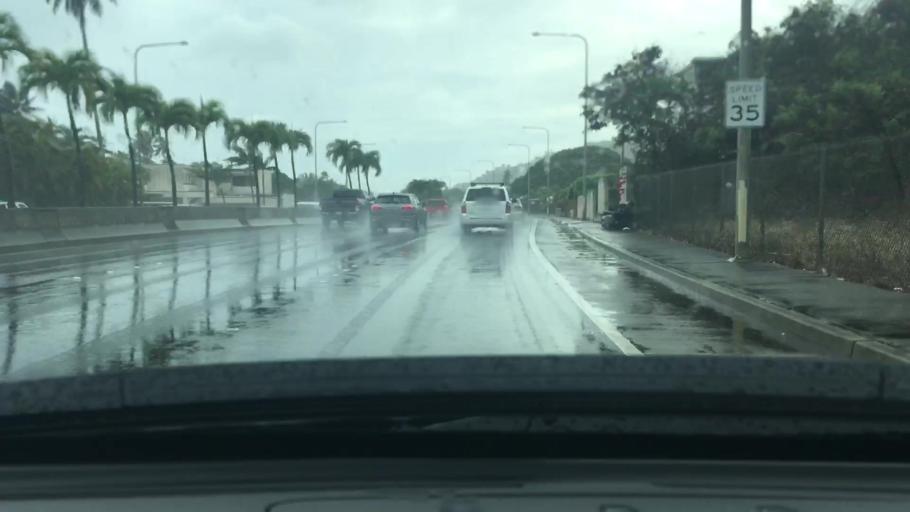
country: US
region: Hawaii
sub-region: Honolulu County
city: Waimanalo Beach
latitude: 21.2827
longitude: -157.7317
